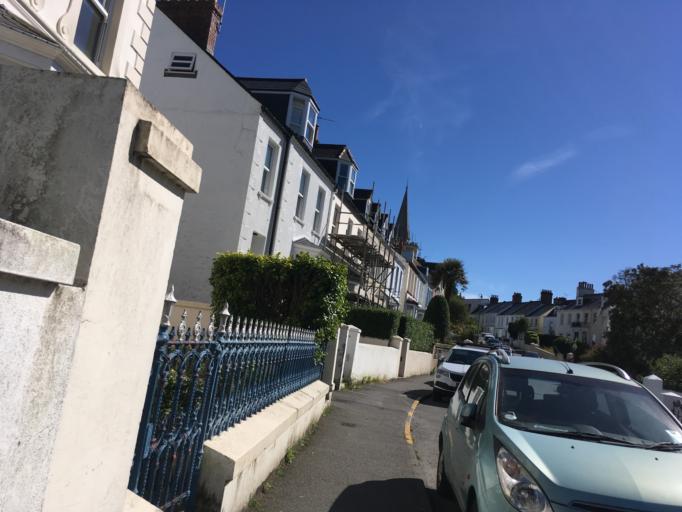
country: GG
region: St Peter Port
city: Saint Peter Port
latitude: 49.4579
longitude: -2.5466
